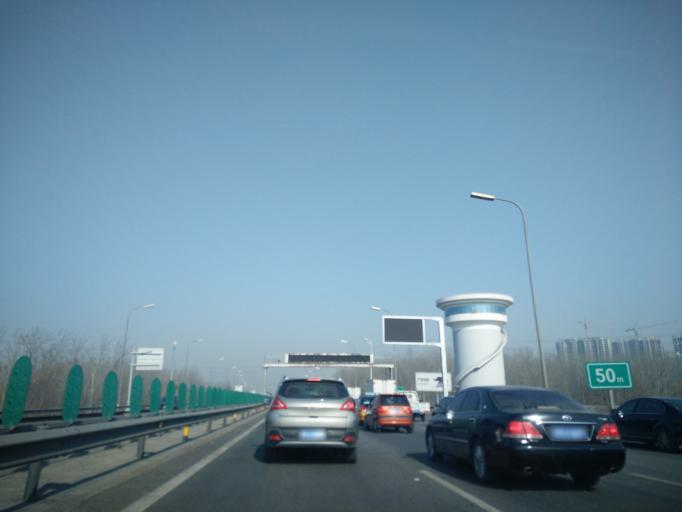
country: CN
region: Beijing
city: Dongba
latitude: 39.9703
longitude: 116.5172
